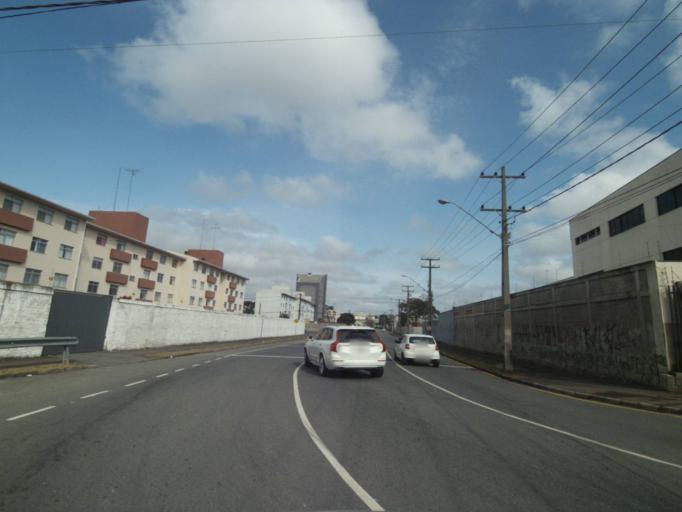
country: BR
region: Parana
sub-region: Curitiba
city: Curitiba
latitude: -25.4672
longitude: -49.2565
